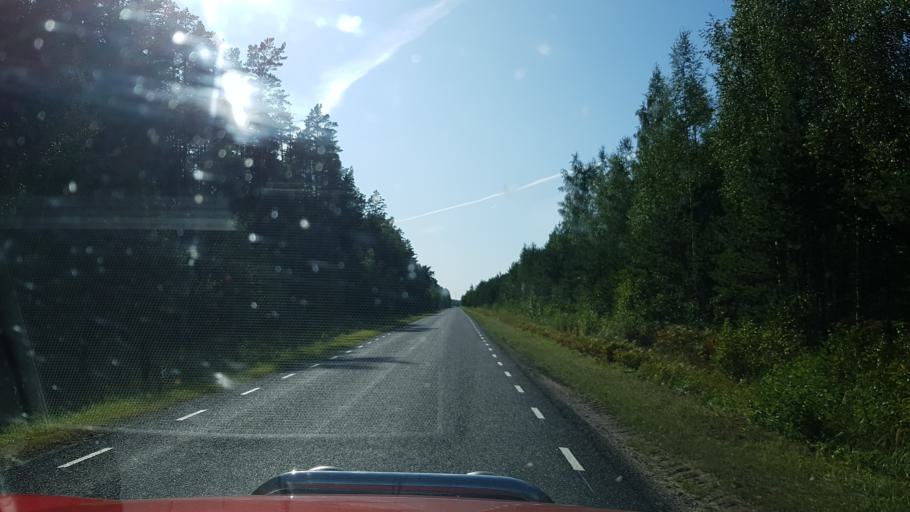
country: LV
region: Salacgrivas
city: Ainazi
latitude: 58.0813
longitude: 24.5567
